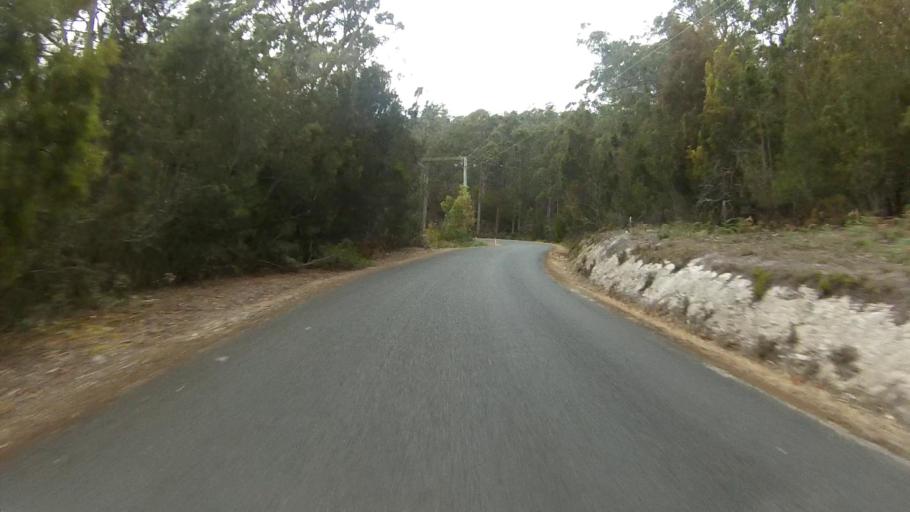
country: AU
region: Tasmania
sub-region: Huon Valley
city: Cygnet
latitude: -43.2157
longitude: 147.1034
